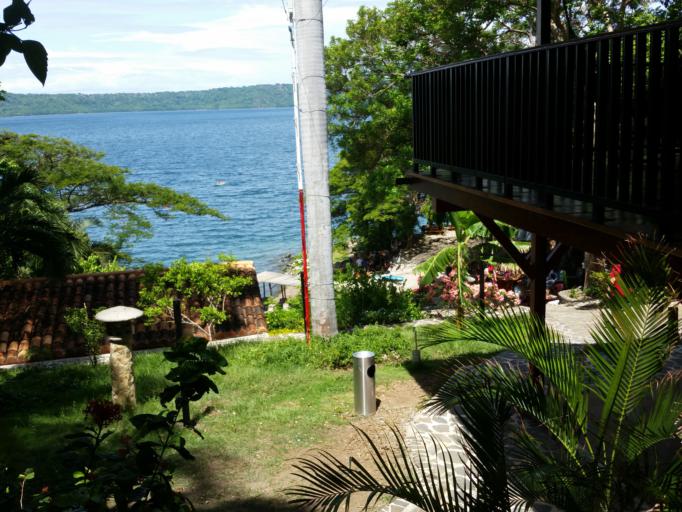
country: NI
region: Masaya
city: Catarina
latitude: 11.9312
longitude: -86.0552
